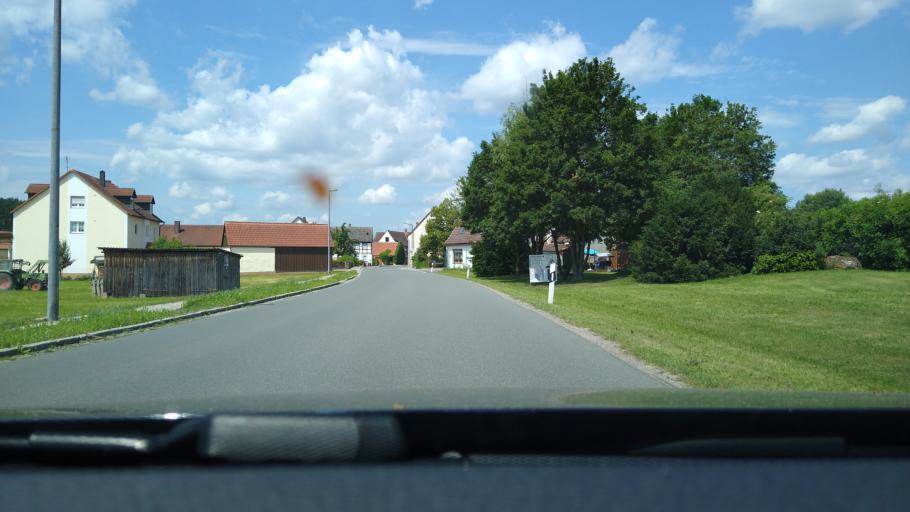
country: DE
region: Bavaria
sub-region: Regierungsbezirk Mittelfranken
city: Trautskirchen
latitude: 49.4553
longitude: 10.5978
